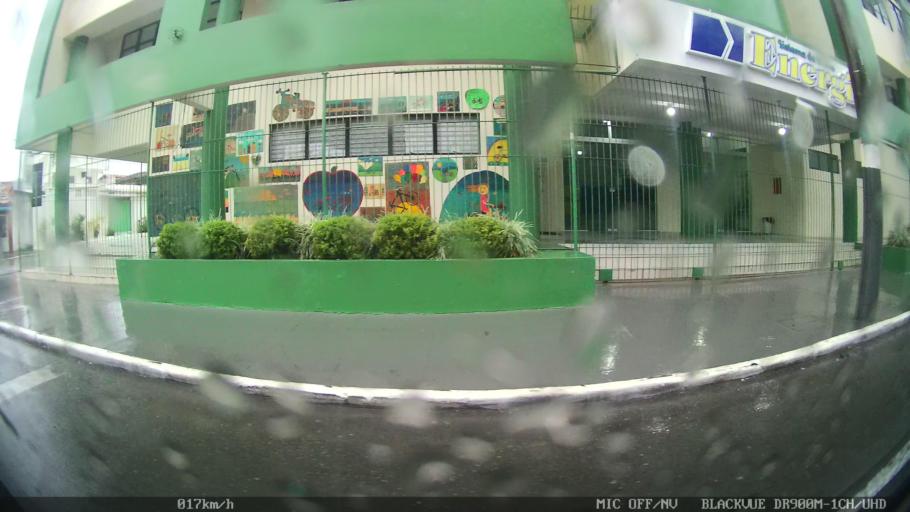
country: BR
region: Santa Catarina
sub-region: Balneario Camboriu
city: Balneario Camboriu
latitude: -26.9981
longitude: -48.6438
